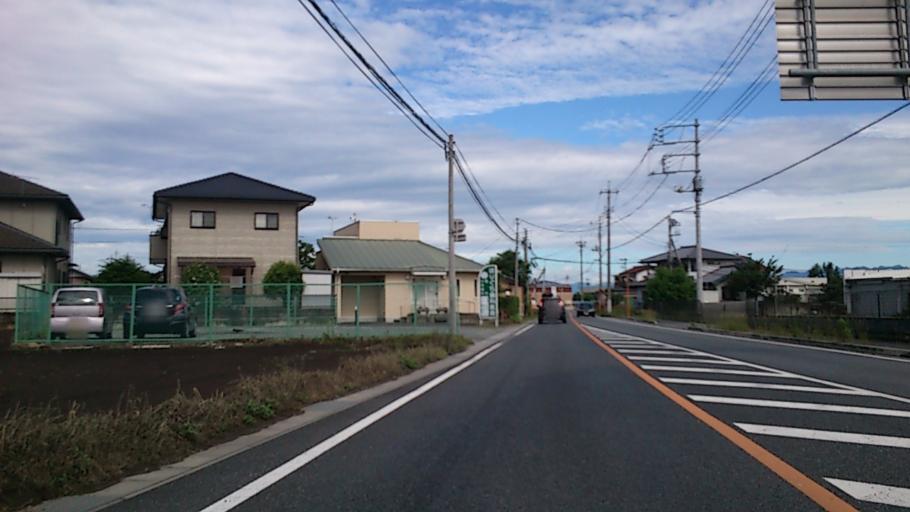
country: JP
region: Gunma
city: Fujioka
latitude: 36.2595
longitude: 139.0878
